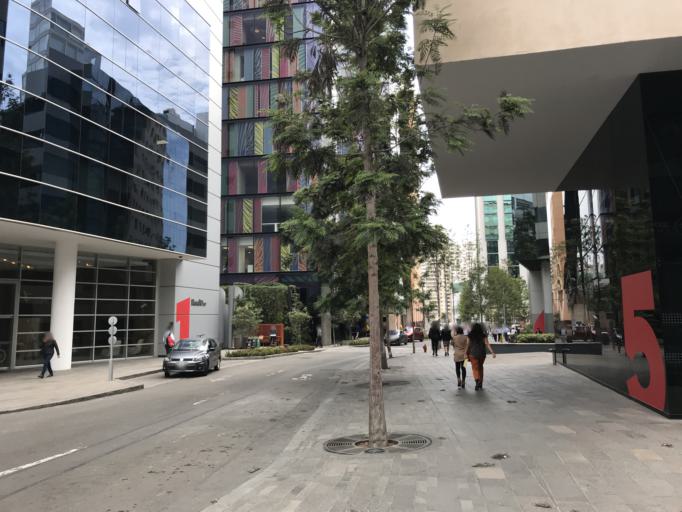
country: PE
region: Lima
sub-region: Lima
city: San Isidro
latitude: -12.0966
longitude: -77.0371
